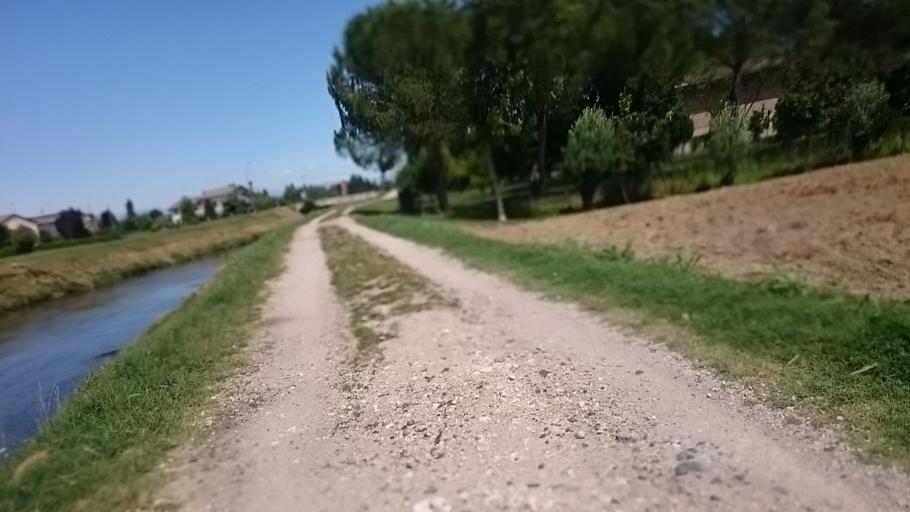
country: IT
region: Veneto
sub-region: Provincia di Padova
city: Codiverno
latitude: 45.4768
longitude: 11.9498
